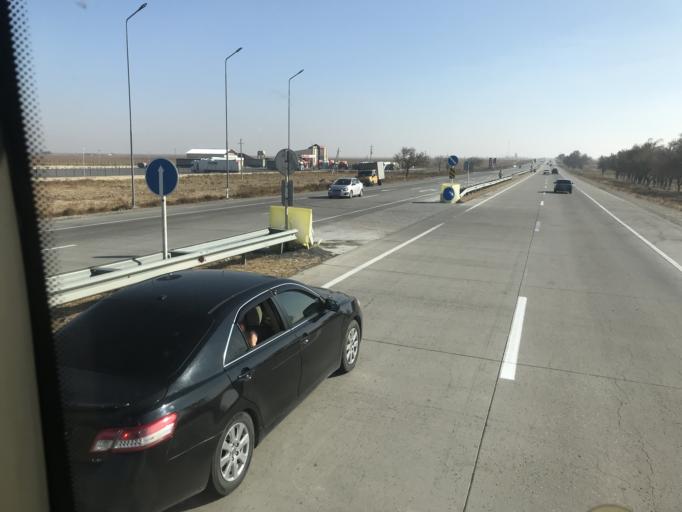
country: KZ
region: Ongtustik Qazaqstan
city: Temirlanovka
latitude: 42.8417
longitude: 69.1033
